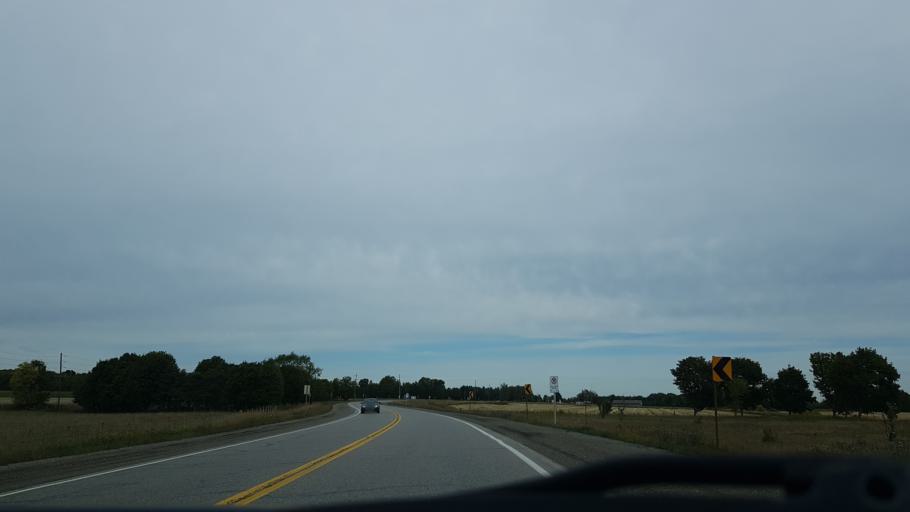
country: CA
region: Ontario
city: Orangeville
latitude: 43.8250
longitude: -80.0351
